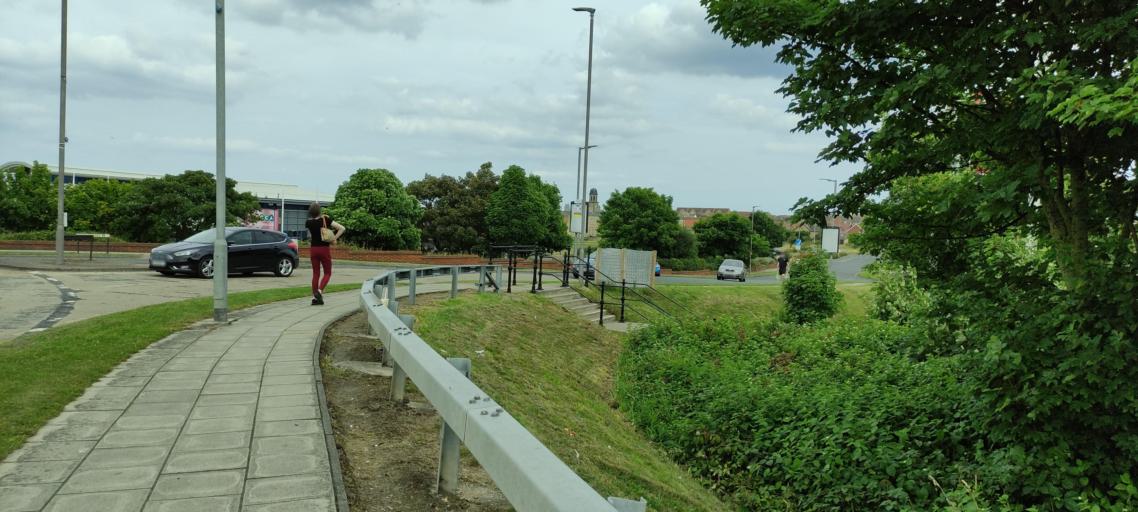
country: GB
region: England
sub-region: Hartlepool
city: Hartlepool
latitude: 54.6877
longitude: -1.2083
